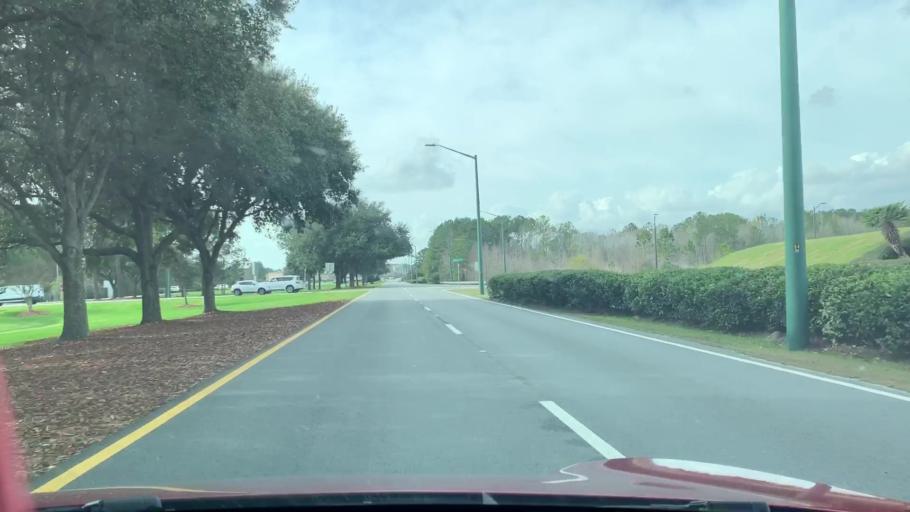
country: US
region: Georgia
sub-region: Chatham County
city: Pooler
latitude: 32.1382
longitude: -81.2260
